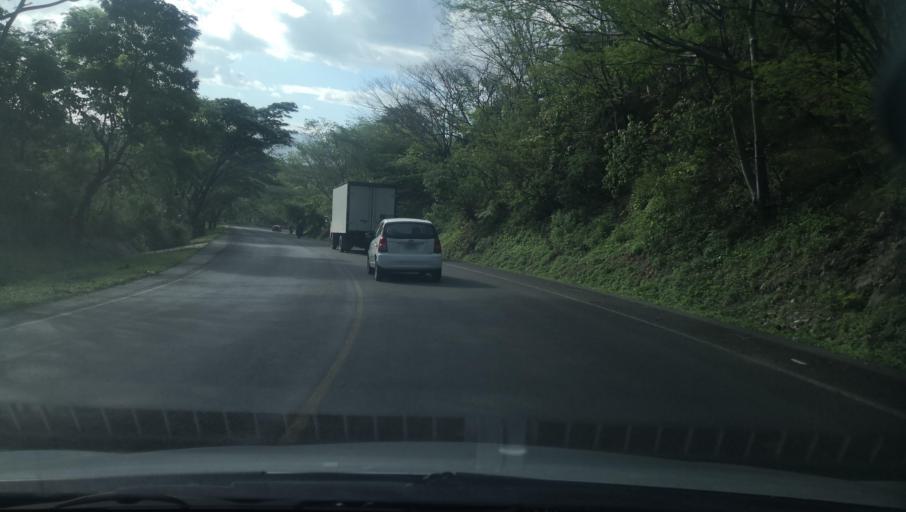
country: NI
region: Nueva Segovia
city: Ocotal
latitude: 13.5979
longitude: -86.4715
